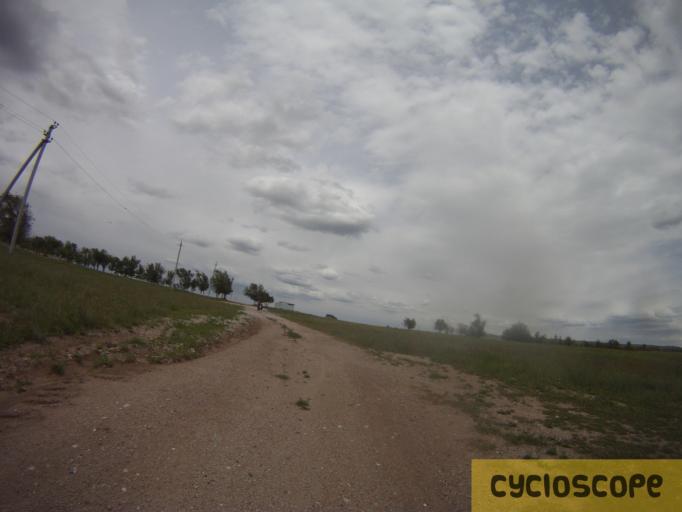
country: KZ
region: Zhambyl
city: Georgiyevka
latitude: 43.3196
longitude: 74.9321
